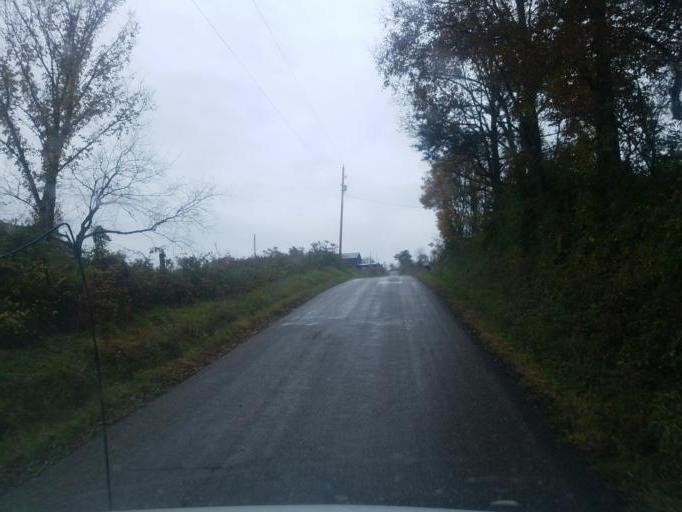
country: US
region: Ohio
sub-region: Washington County
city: Belpre
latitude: 39.3180
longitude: -81.6043
